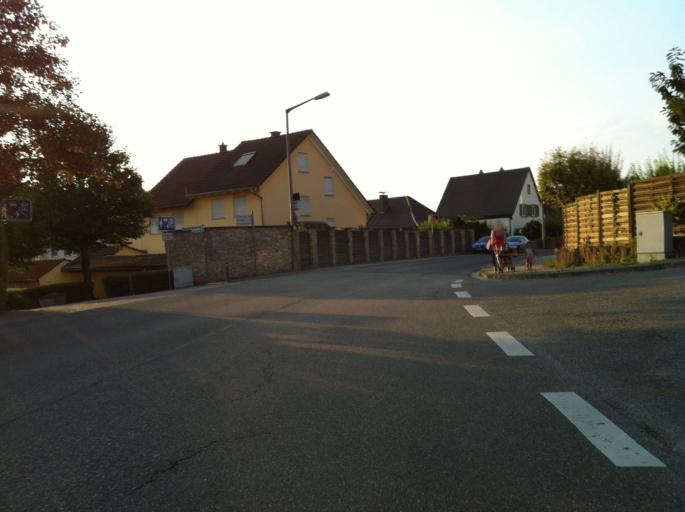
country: DE
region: Rheinland-Pfalz
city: Schwabenheim
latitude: 49.9272
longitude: 8.0995
